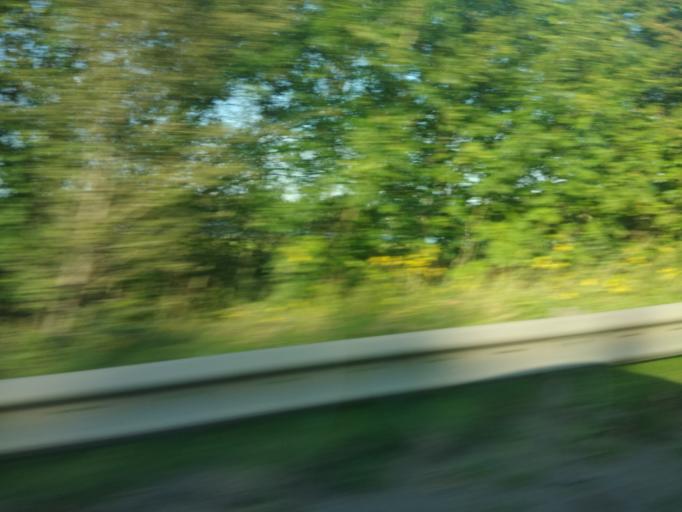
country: GB
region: England
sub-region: Derbyshire
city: Pilsley
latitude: 53.2053
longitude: -1.3715
